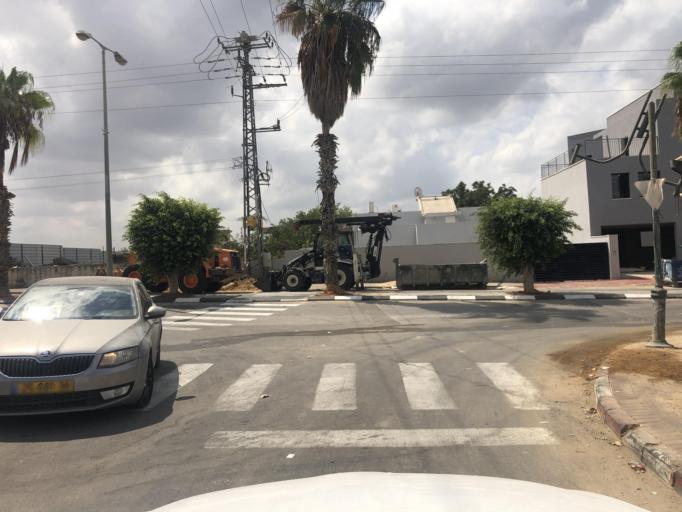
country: IL
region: Central District
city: Jaljulya
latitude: 32.1525
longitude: 34.9573
